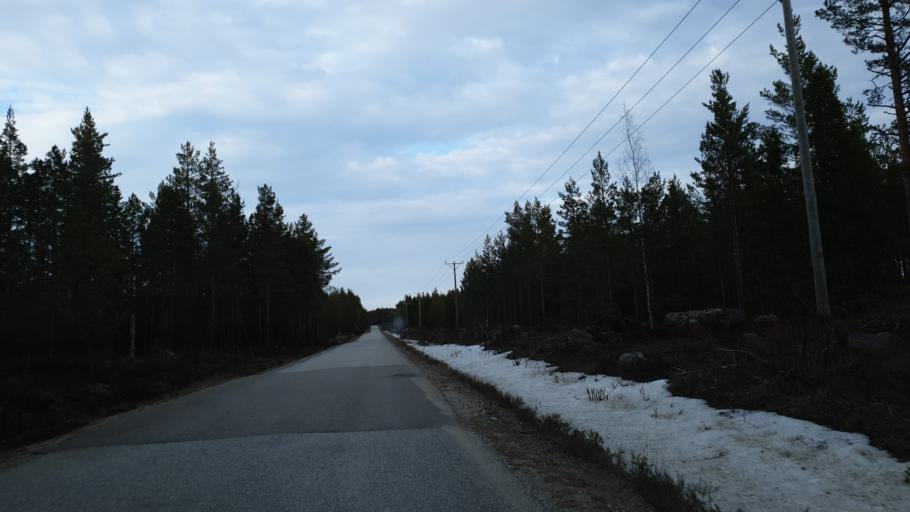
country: SE
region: Vaesternorrland
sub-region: Sundsvalls Kommun
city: Njurundabommen
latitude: 61.9918
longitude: 17.3800
